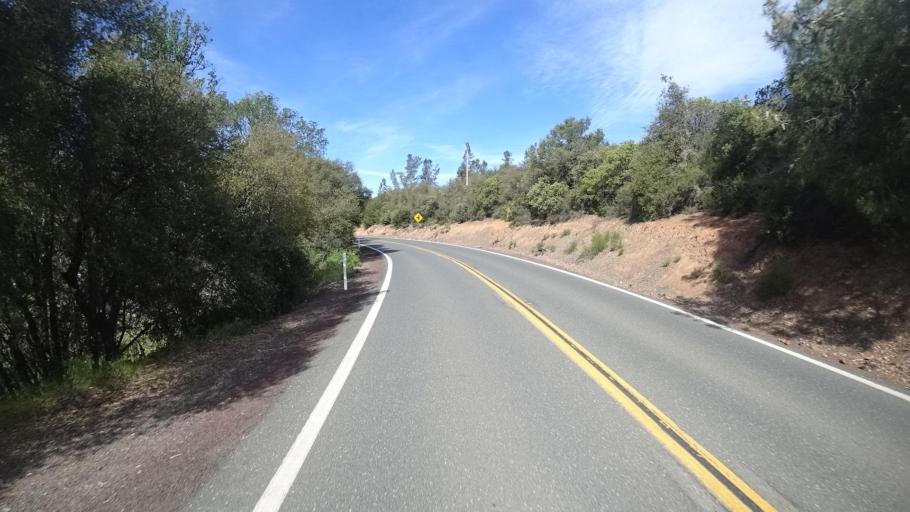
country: US
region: California
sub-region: Lake County
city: Cobb
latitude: 38.9081
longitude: -122.7623
